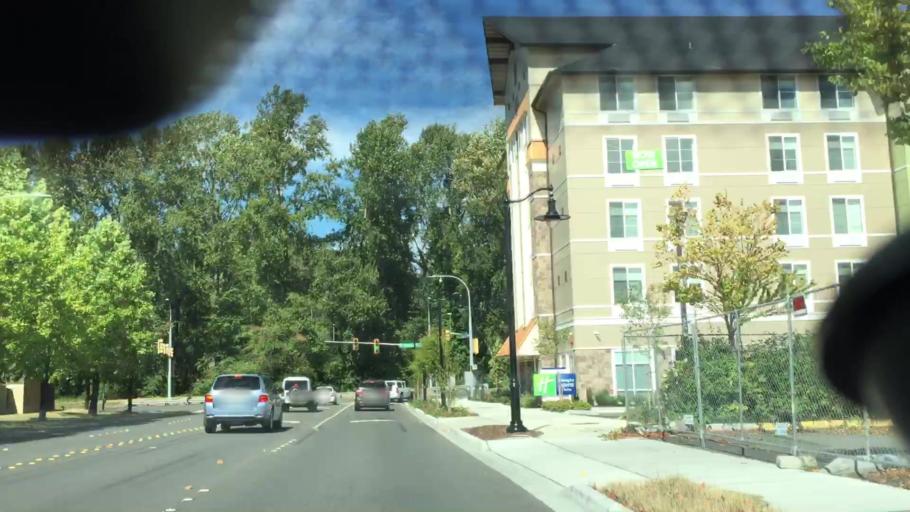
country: US
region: Washington
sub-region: King County
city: Tukwila
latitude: 47.4606
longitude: -122.2500
